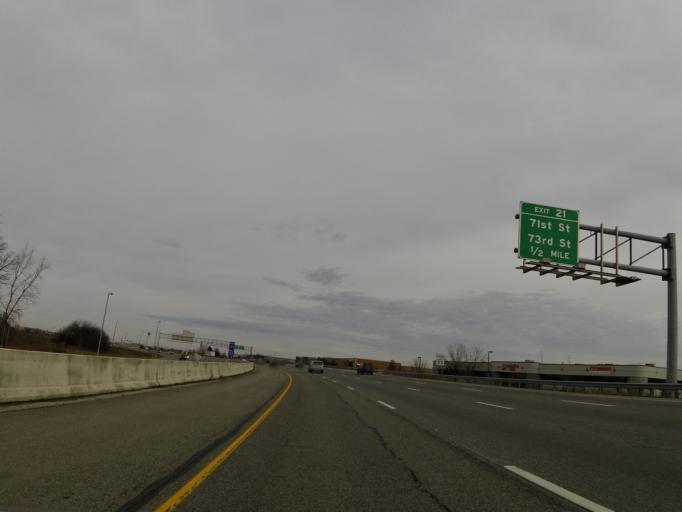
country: US
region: Indiana
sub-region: Marion County
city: Speedway
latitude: 39.8683
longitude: -86.2694
